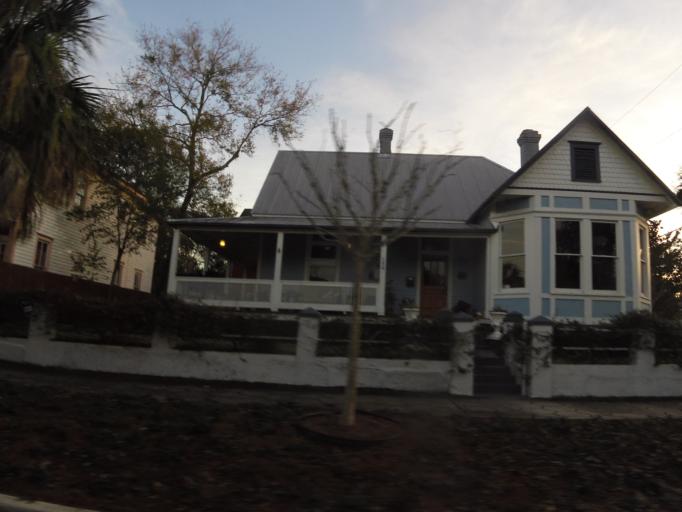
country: US
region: Florida
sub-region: Duval County
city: Jacksonville
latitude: 30.3419
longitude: -81.6574
